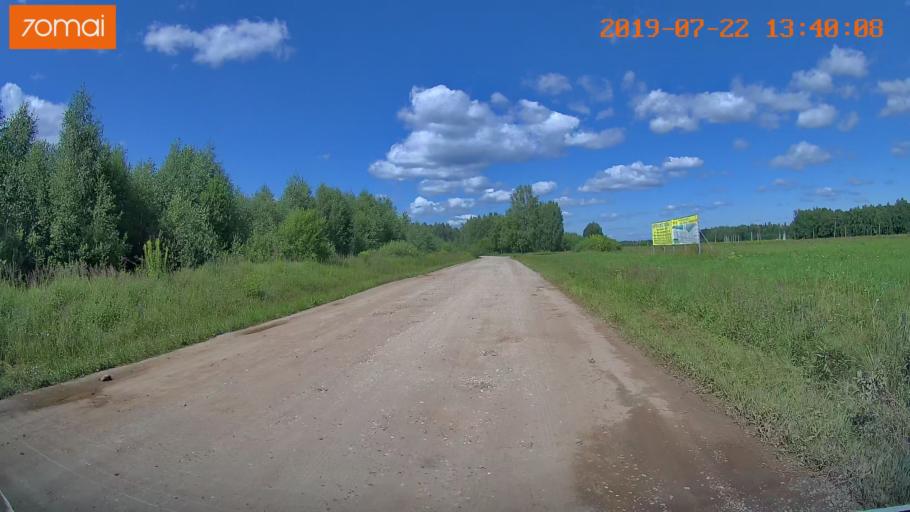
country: RU
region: Ivanovo
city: Novo-Talitsy
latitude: 57.0752
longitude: 40.8813
